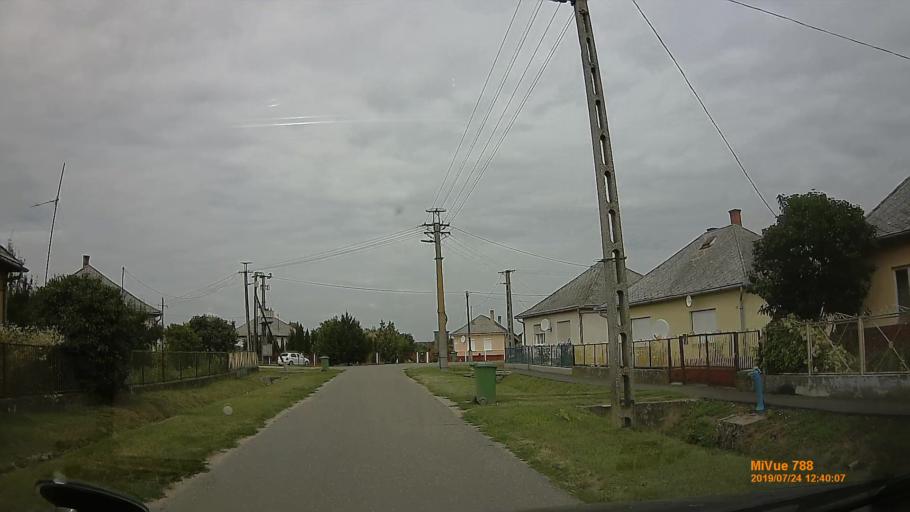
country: HU
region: Szabolcs-Szatmar-Bereg
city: Aranyosapati
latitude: 48.1902
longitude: 22.3126
